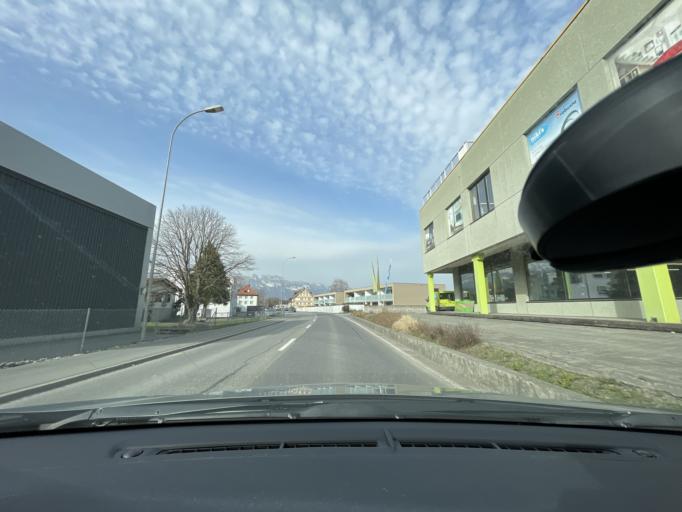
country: CH
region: Saint Gallen
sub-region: Wahlkreis Werdenberg
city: Sevelen
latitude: 47.1431
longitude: 9.4859
